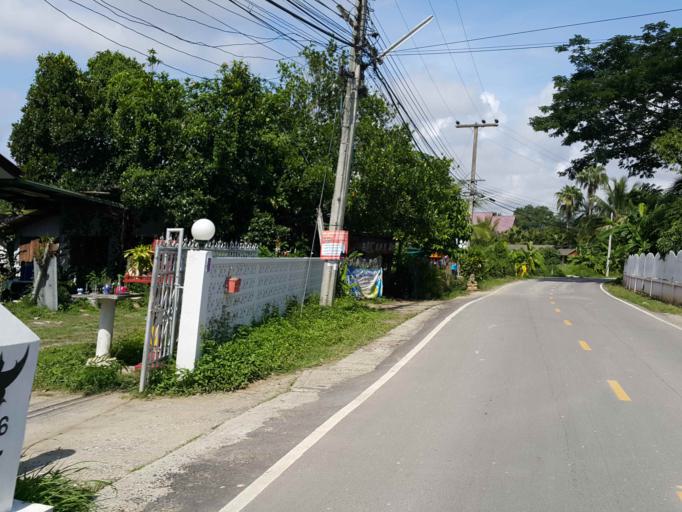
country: TH
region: Chiang Mai
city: San Sai
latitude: 18.8033
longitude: 99.0674
